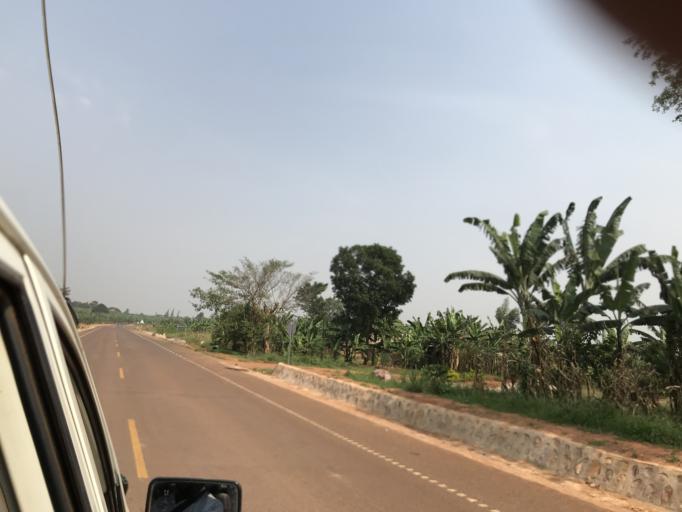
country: UG
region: Central Region
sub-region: Kalungu District
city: Kalungu
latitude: -0.2277
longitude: 31.7270
